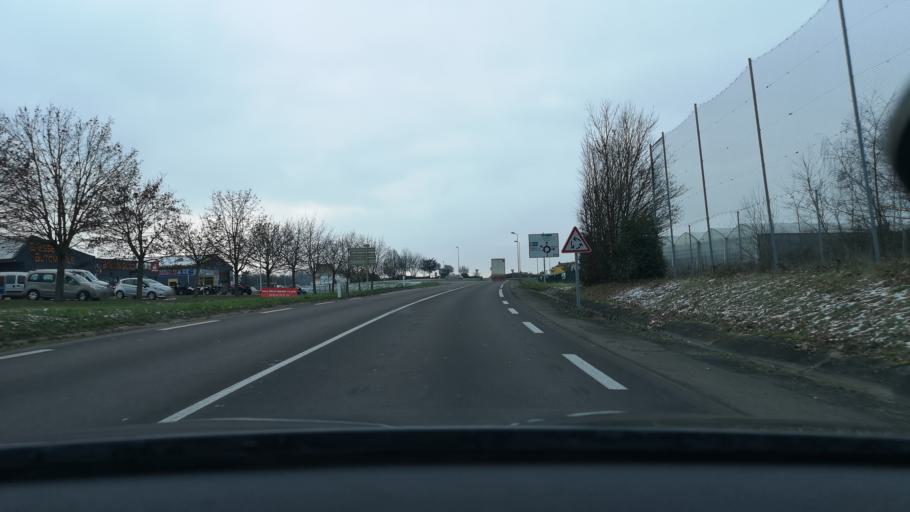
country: FR
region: Bourgogne
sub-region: Departement de Saone-et-Loire
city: Saint-Marcel
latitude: 46.7866
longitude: 4.9076
